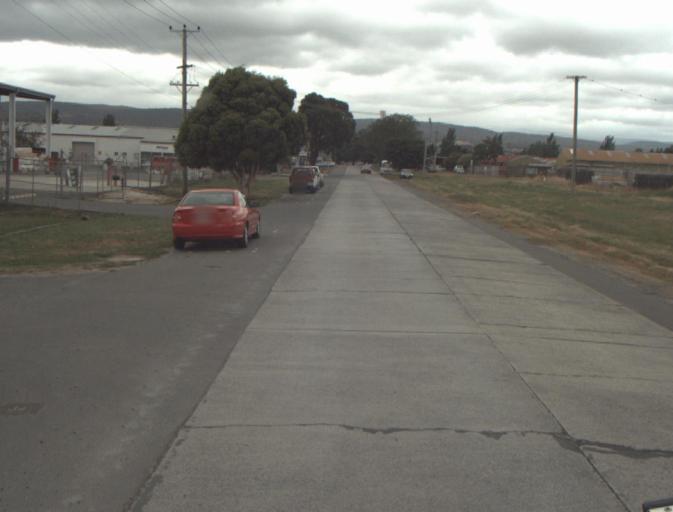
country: AU
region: Tasmania
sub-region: Launceston
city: Launceston
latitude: -41.4283
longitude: 147.1279
